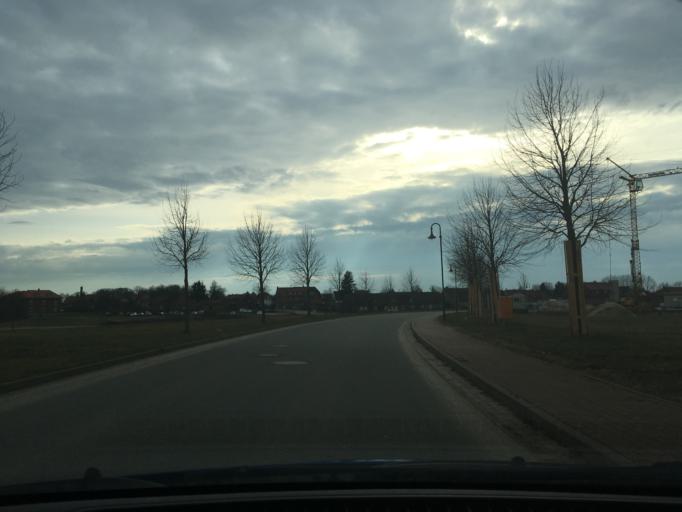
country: DE
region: Mecklenburg-Vorpommern
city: Zarrentin
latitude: 53.5577
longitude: 10.9177
